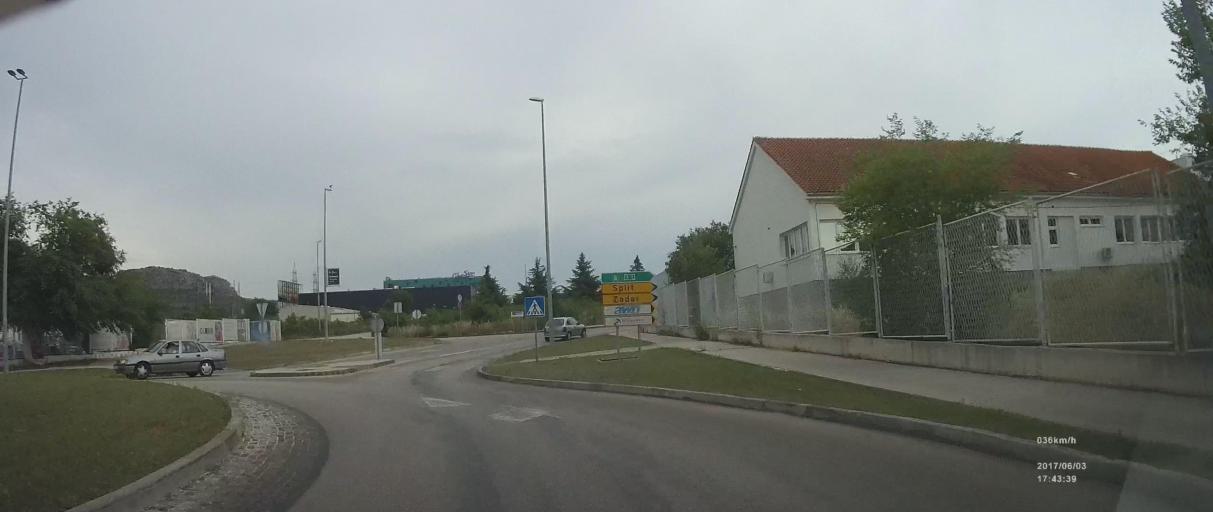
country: HR
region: Sibensko-Kniniska
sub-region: Grad Sibenik
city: Sibenik
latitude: 43.7144
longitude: 15.9086
